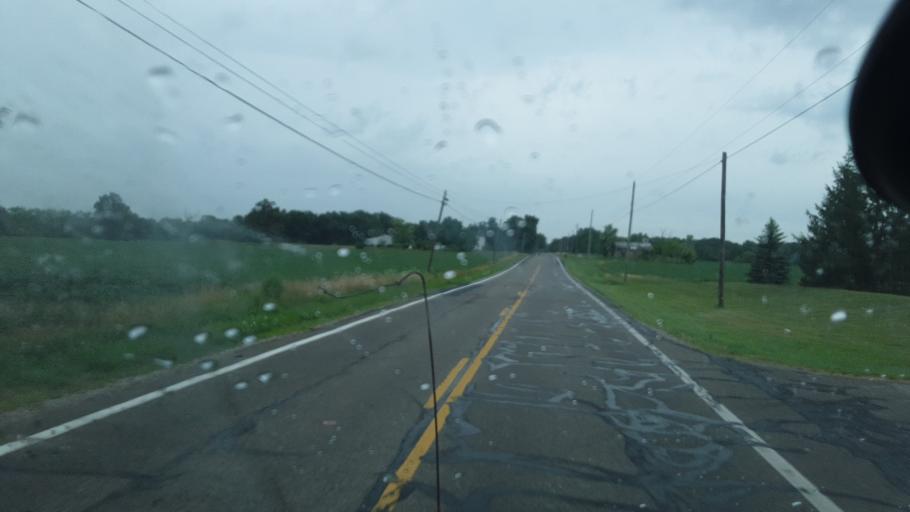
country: US
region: Ohio
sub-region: Williams County
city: Bryan
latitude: 41.4776
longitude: -84.6131
